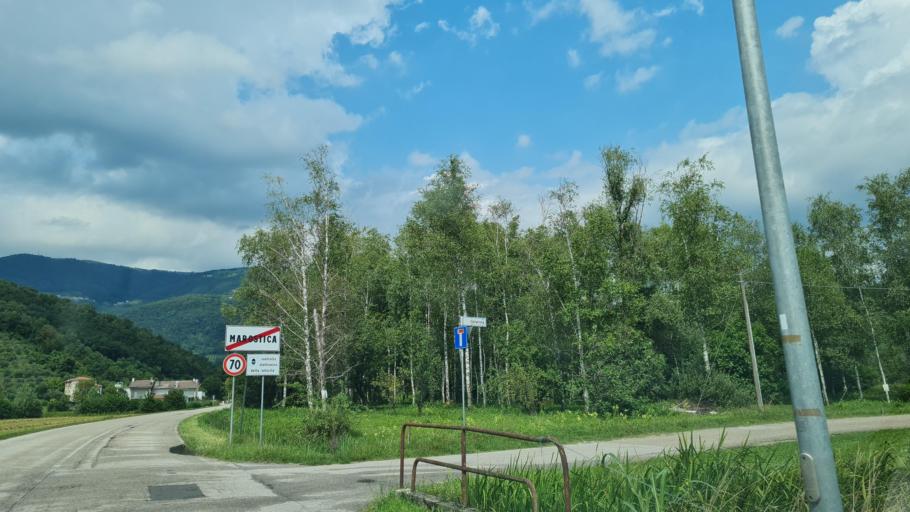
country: IT
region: Veneto
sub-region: Provincia di Vicenza
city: Marostica
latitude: 45.7562
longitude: 11.6605
